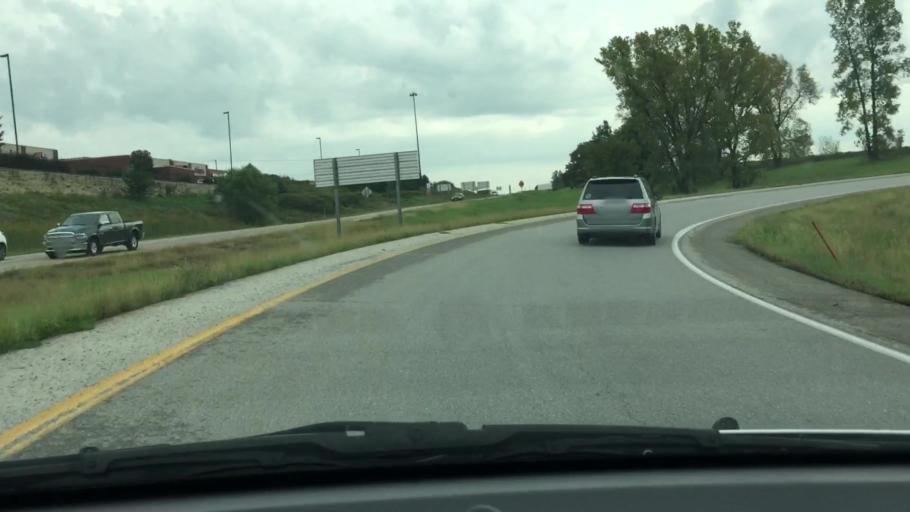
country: US
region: Iowa
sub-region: Johnson County
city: Coralville
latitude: 41.6956
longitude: -91.6067
